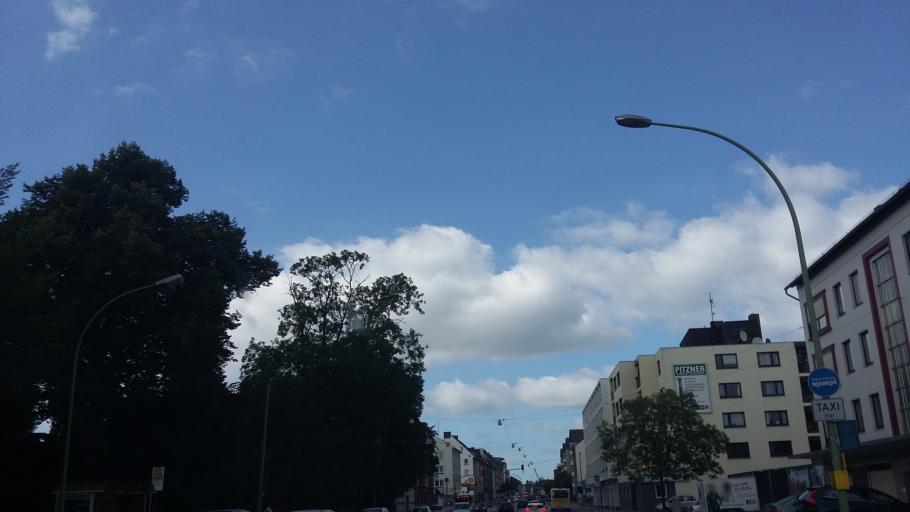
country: DE
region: Bremen
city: Bremerhaven
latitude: 53.5255
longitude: 8.5901
